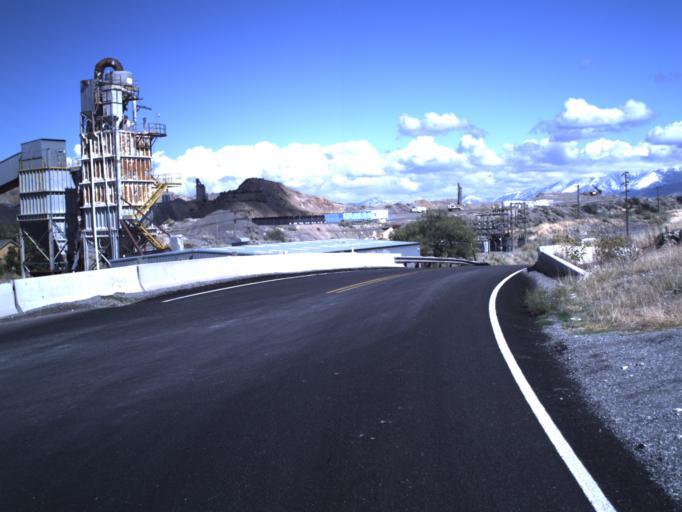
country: US
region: Utah
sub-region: Utah County
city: Genola
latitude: 40.0041
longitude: -111.8125
